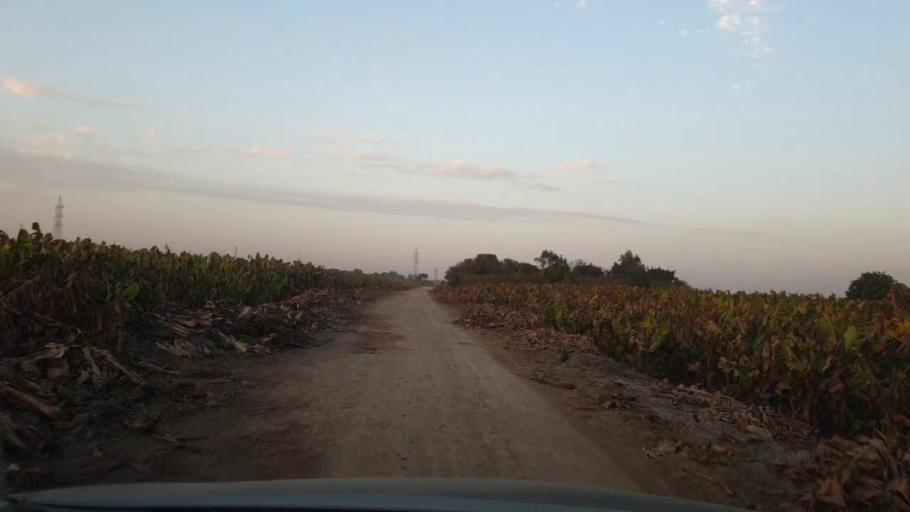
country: PK
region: Sindh
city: Matiari
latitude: 25.6127
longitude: 68.4834
